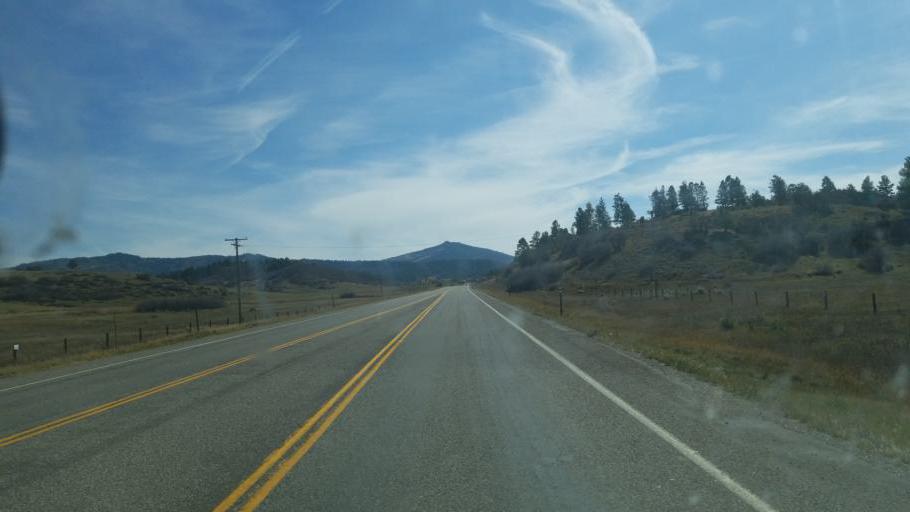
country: US
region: New Mexico
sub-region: Rio Arriba County
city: Dulce
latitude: 37.0134
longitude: -106.8052
